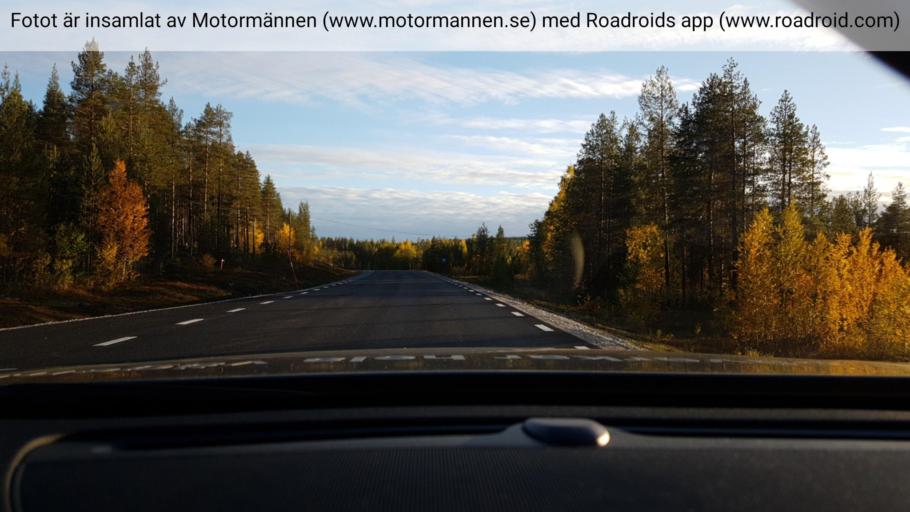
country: SE
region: Norrbotten
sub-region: Jokkmokks Kommun
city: Jokkmokk
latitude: 66.5917
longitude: 19.8040
